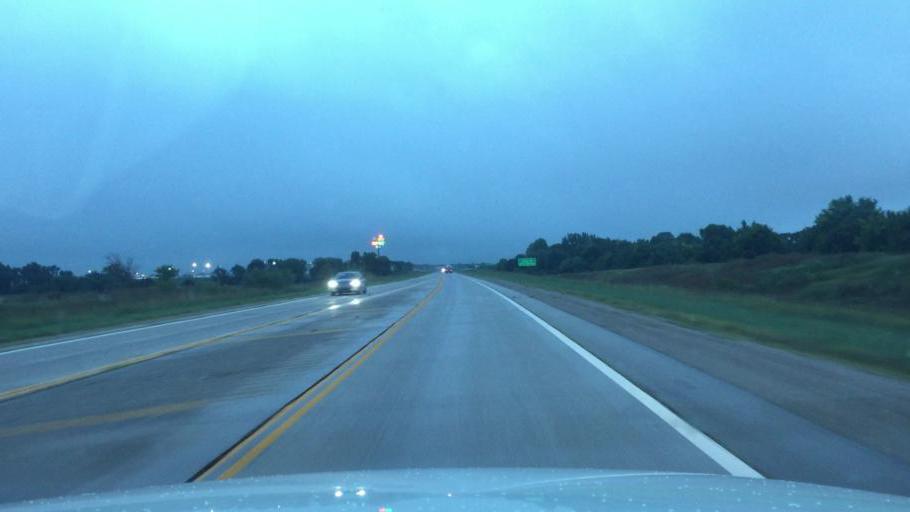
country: US
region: Kansas
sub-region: Neosho County
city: Chanute
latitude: 37.6567
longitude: -95.4797
